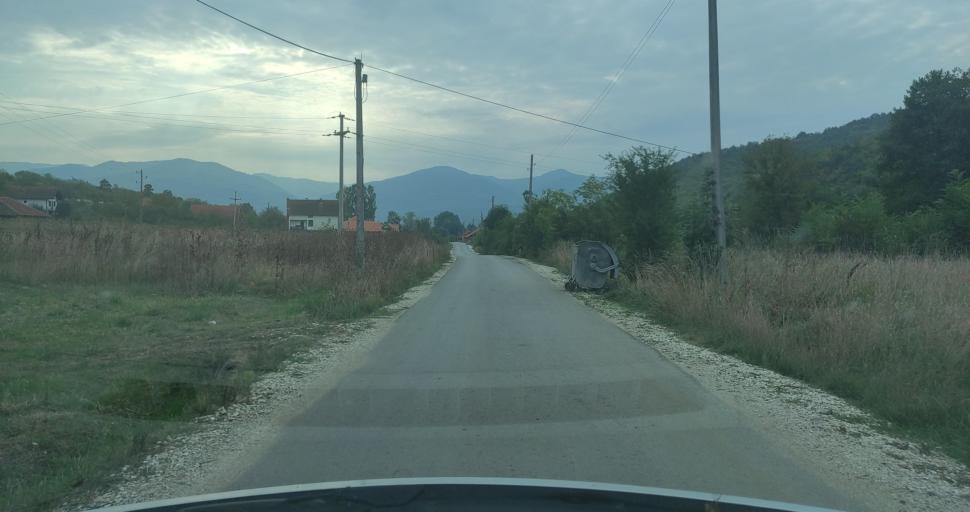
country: RS
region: Central Serbia
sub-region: Pcinjski Okrug
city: Vladicin Han
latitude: 42.6692
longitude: 22.0305
